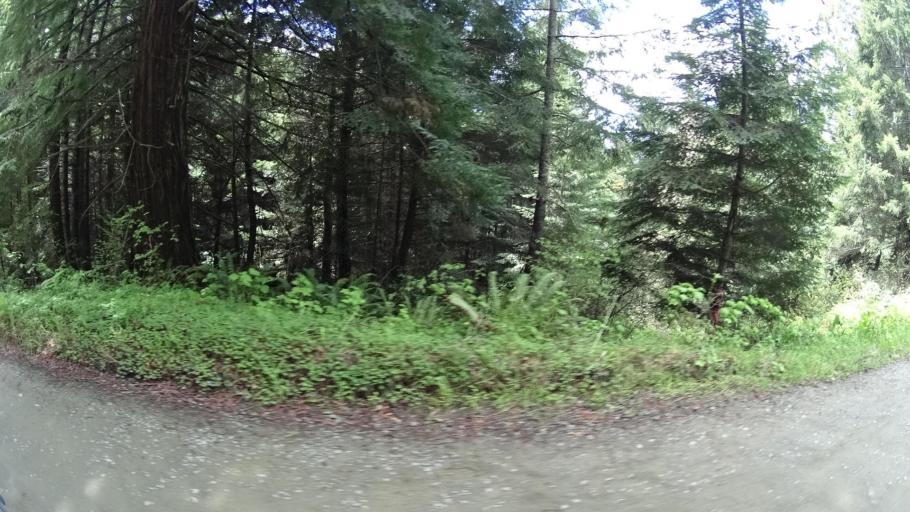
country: US
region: California
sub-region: Humboldt County
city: Blue Lake
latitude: 40.8078
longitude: -123.8839
